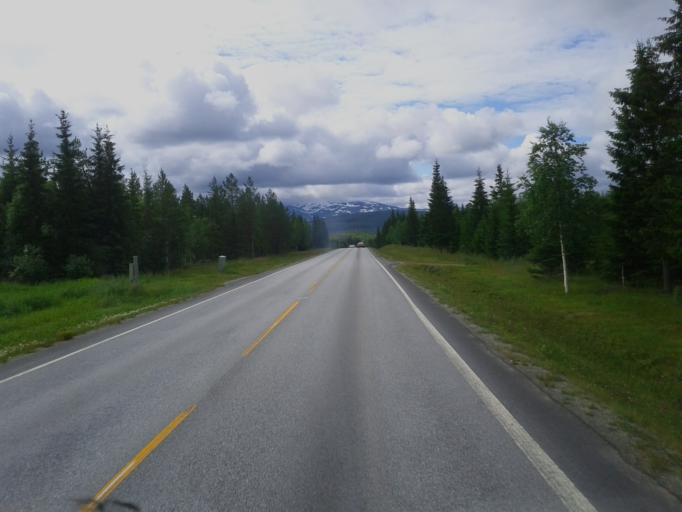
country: NO
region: Nord-Trondelag
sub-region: Namsskogan
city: Namsskogan
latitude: 64.7202
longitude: 12.8009
